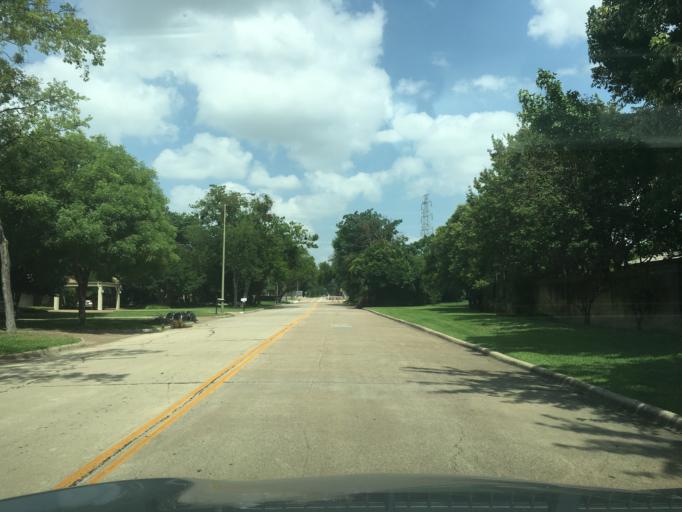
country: US
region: Texas
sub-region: Dallas County
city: University Park
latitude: 32.9022
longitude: -96.8151
